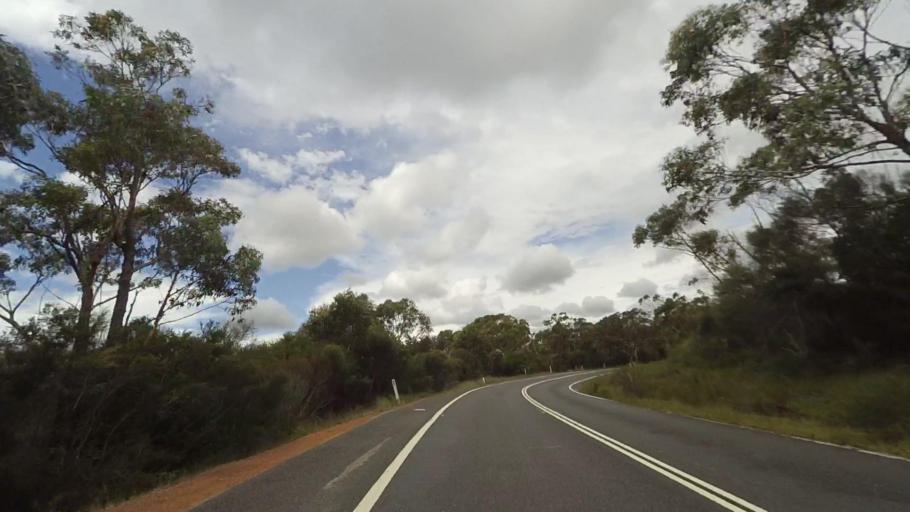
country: AU
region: New South Wales
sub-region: Sutherland Shire
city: Grays Point
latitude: -34.0824
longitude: 151.0631
